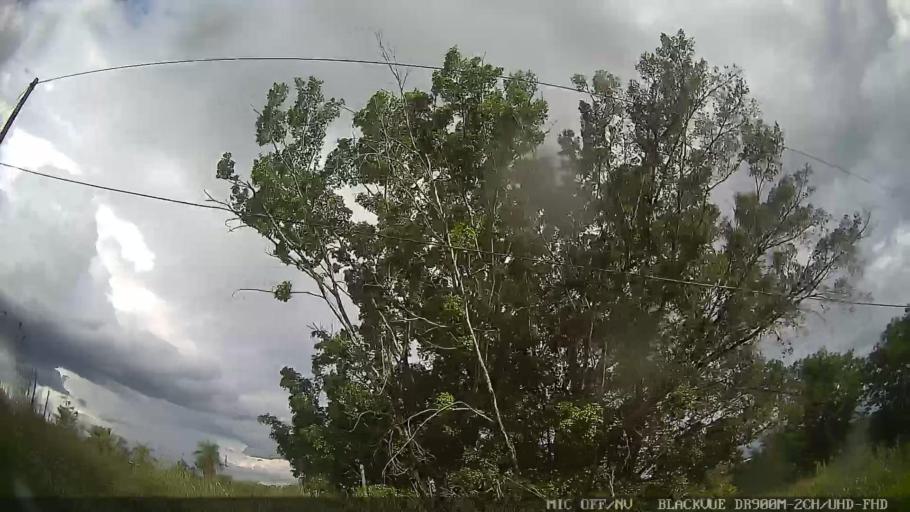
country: BR
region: Sao Paulo
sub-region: Jaguariuna
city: Jaguariuna
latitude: -22.6666
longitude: -47.0327
